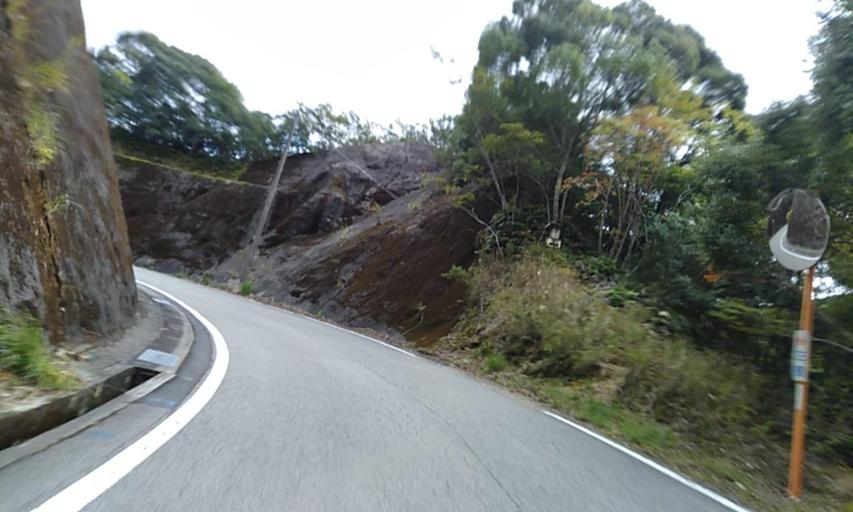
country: JP
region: Wakayama
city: Shingu
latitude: 33.5428
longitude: 135.8332
